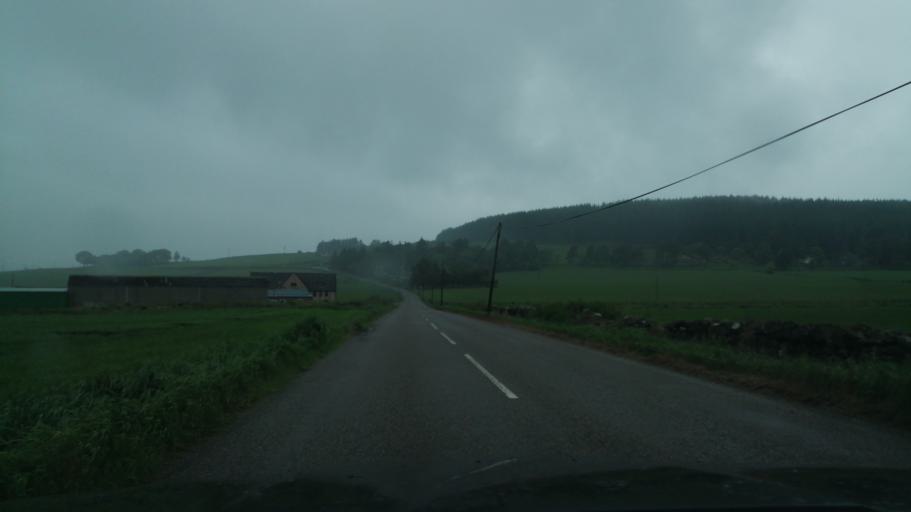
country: GB
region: Scotland
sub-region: Aberdeenshire
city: Huntly
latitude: 57.5468
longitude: -2.8163
